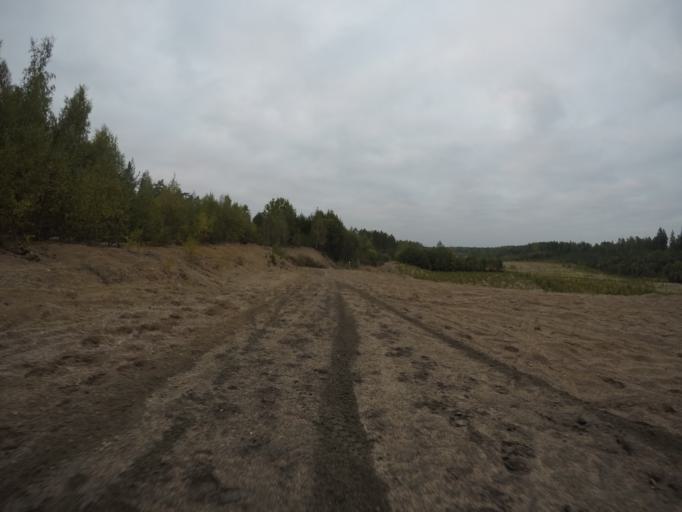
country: SE
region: Vaestmanland
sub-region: Kungsors Kommun
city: Kungsoer
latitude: 59.3820
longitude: 16.1090
